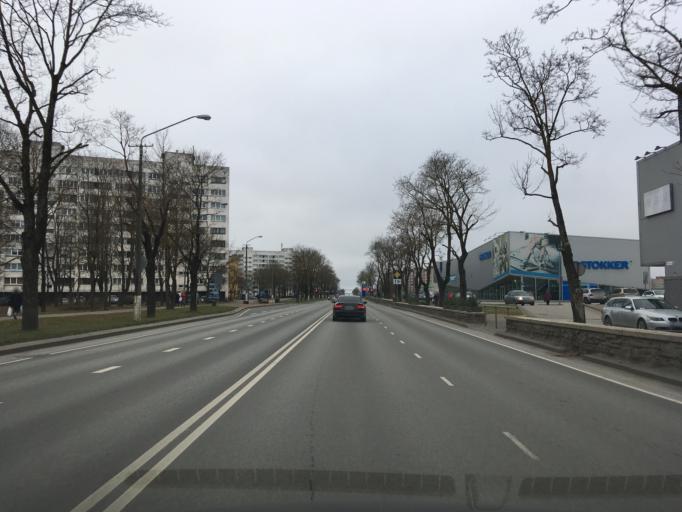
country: EE
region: Ida-Virumaa
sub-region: Narva linn
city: Narva
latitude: 59.3811
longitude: 28.1729
